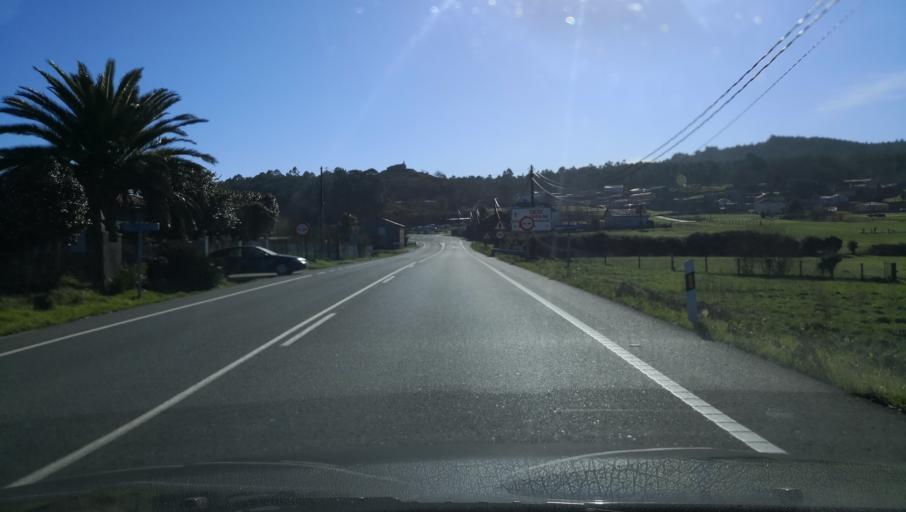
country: ES
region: Galicia
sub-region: Provincia da Coruna
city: Ribeira
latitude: 42.7497
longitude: -8.3483
